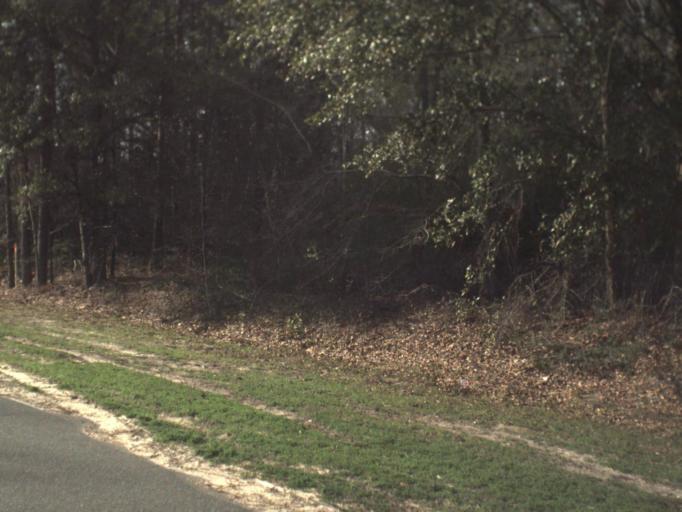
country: US
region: Florida
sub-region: Bay County
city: Youngstown
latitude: 30.4352
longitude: -85.3926
